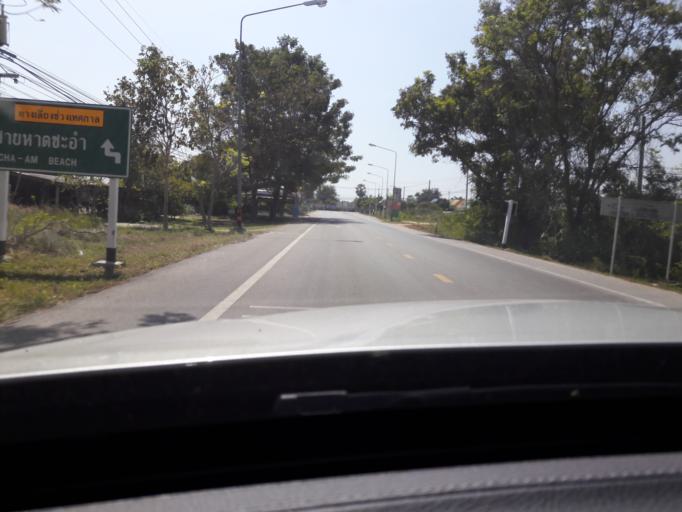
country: TH
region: Phetchaburi
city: Cha-am
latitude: 12.8264
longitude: 99.9850
